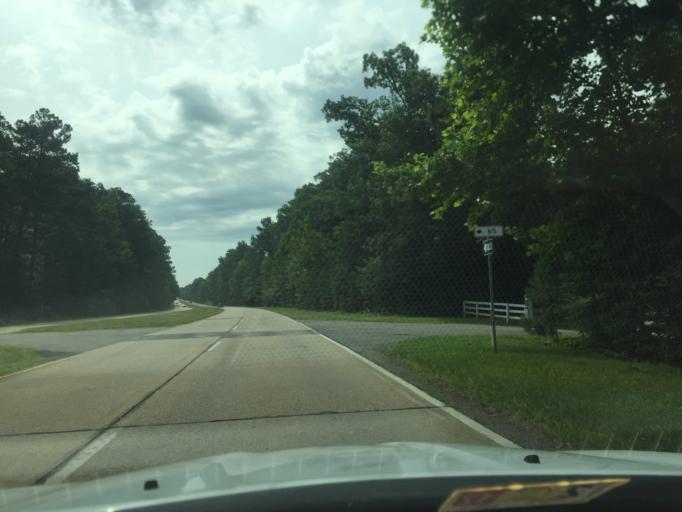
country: US
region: Virginia
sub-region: Charles City County
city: Charles City
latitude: 37.4594
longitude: -77.0979
